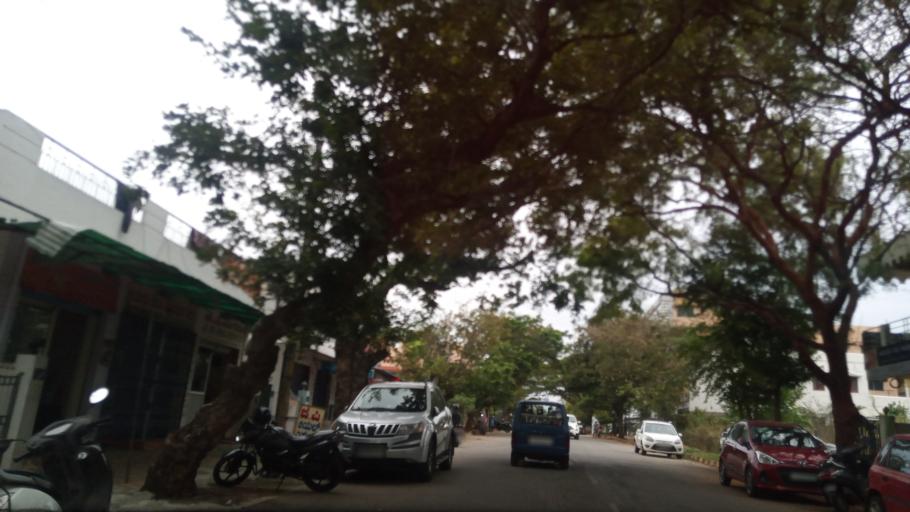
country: IN
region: Karnataka
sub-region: Mysore
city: Mysore
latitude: 12.2884
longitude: 76.6173
